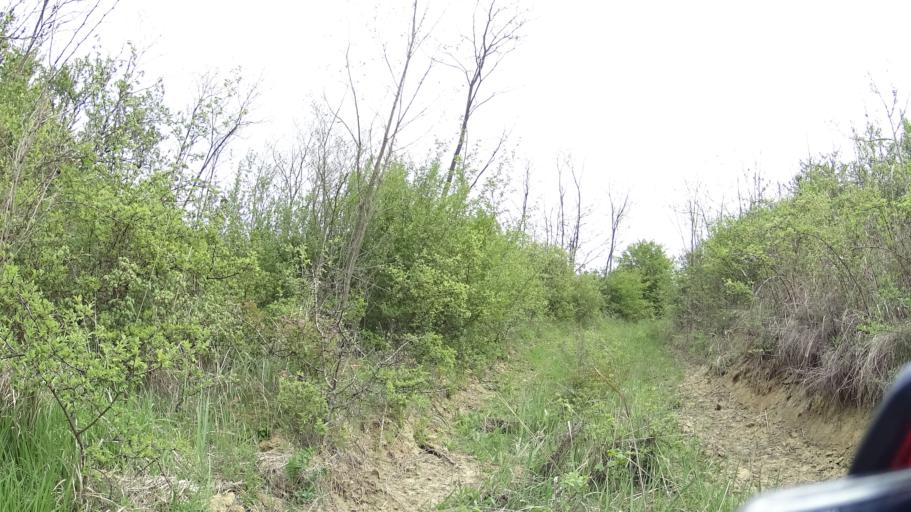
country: HU
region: Pest
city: Kosd
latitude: 47.8170
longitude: 19.2593
